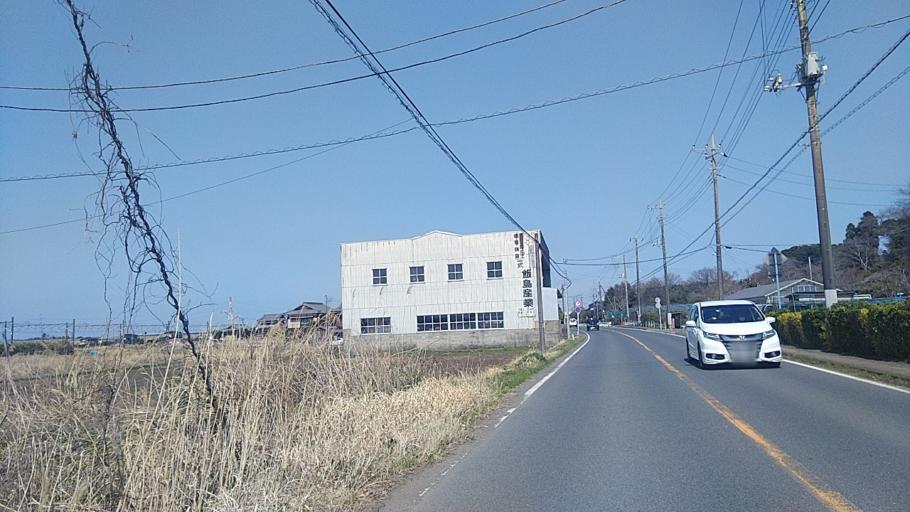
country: JP
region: Ibaraki
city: Edosaki
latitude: 35.8729
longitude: 140.3461
